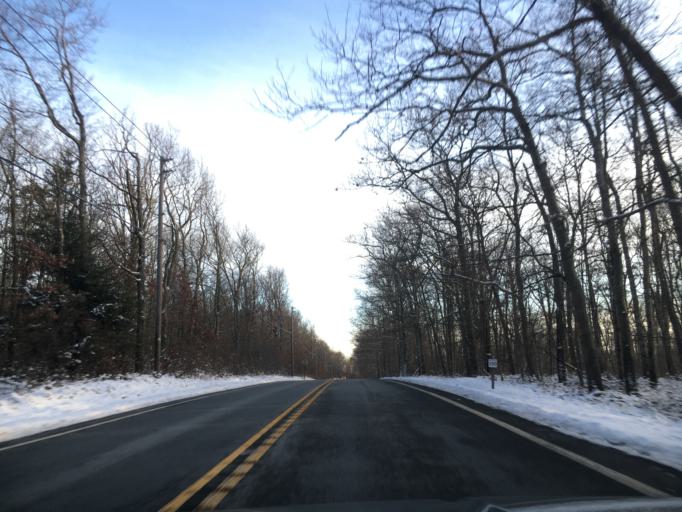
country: US
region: Pennsylvania
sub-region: Pike County
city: Hemlock Farms
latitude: 41.2712
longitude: -75.0862
